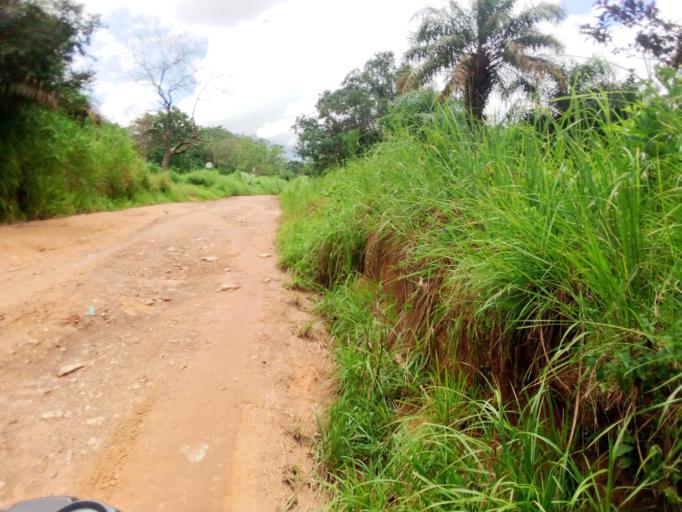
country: SL
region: Eastern Province
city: Simbakoro
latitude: 8.6088
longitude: -10.9846
